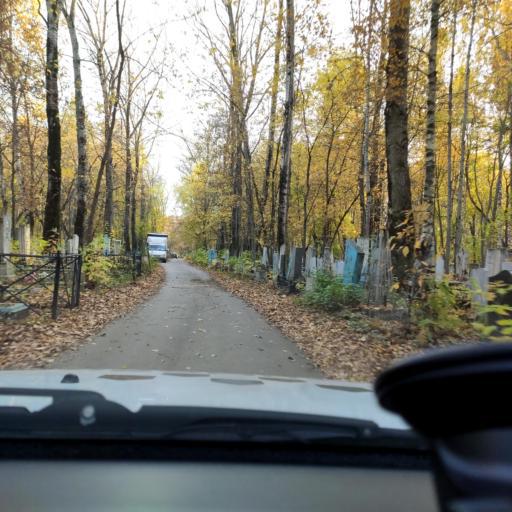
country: RU
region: Perm
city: Perm
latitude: 57.9922
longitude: 56.2814
